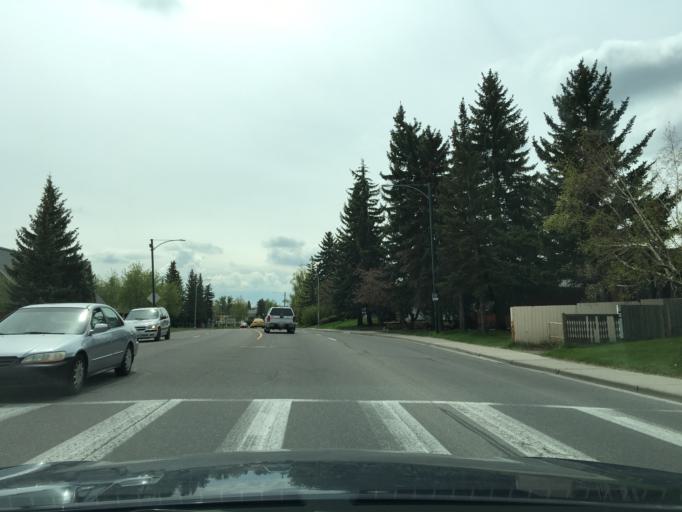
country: CA
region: Alberta
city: Calgary
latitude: 50.9591
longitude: -114.0848
